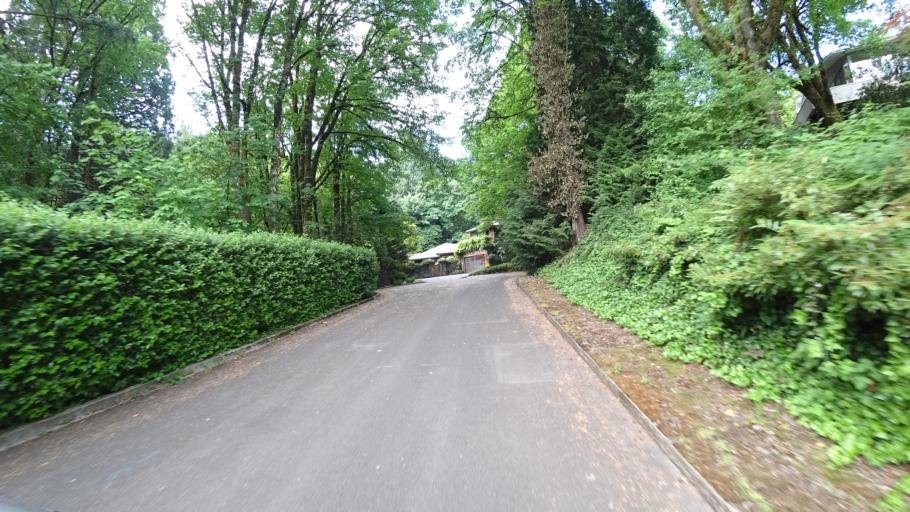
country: US
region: Oregon
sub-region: Multnomah County
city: Portland
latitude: 45.5024
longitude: -122.7097
